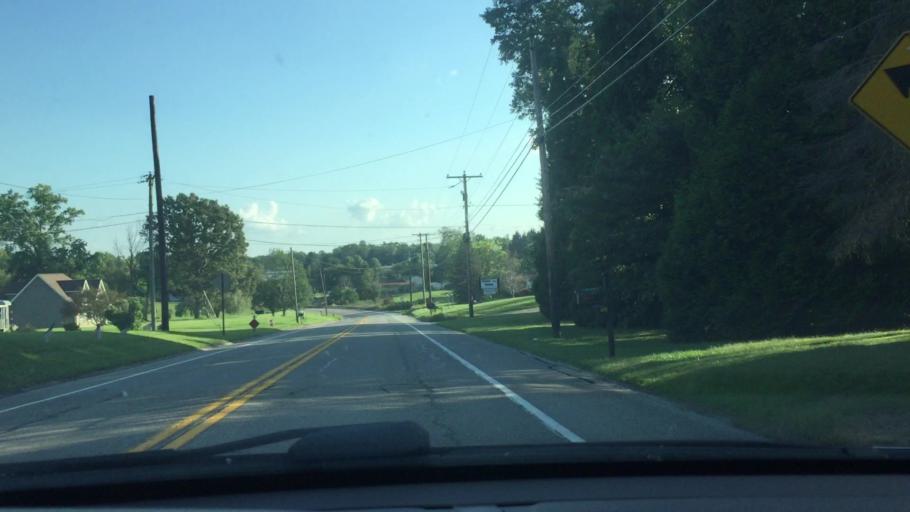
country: US
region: Pennsylvania
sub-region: Mercer County
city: Grove City
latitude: 41.1865
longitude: -80.0837
